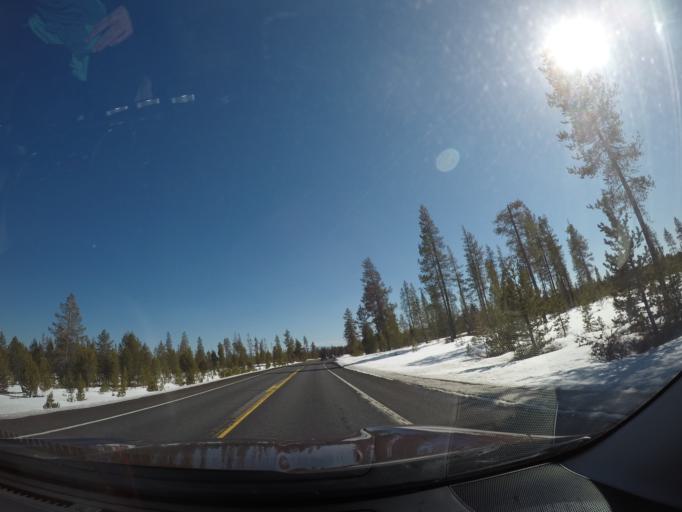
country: US
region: Oregon
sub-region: Deschutes County
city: Three Rivers
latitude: 43.8692
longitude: -121.5465
